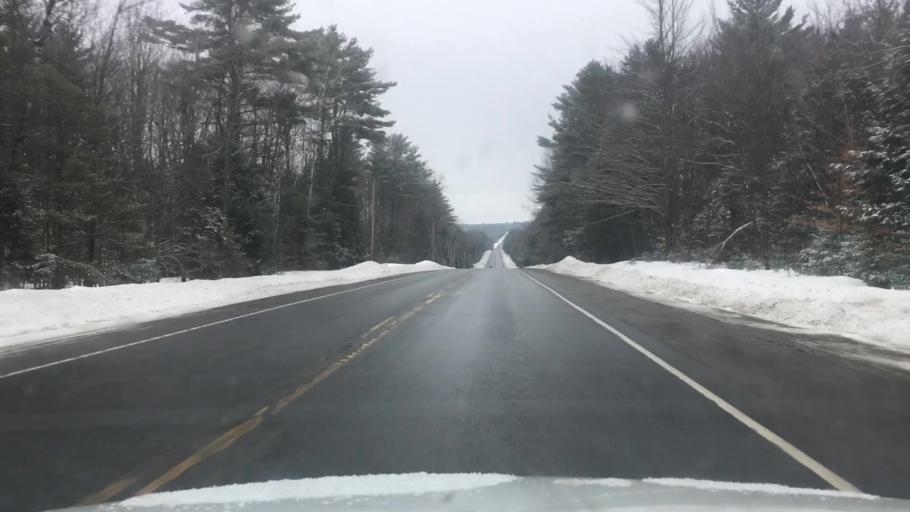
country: US
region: Maine
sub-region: Franklin County
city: New Sharon
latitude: 44.6399
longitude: -69.9931
